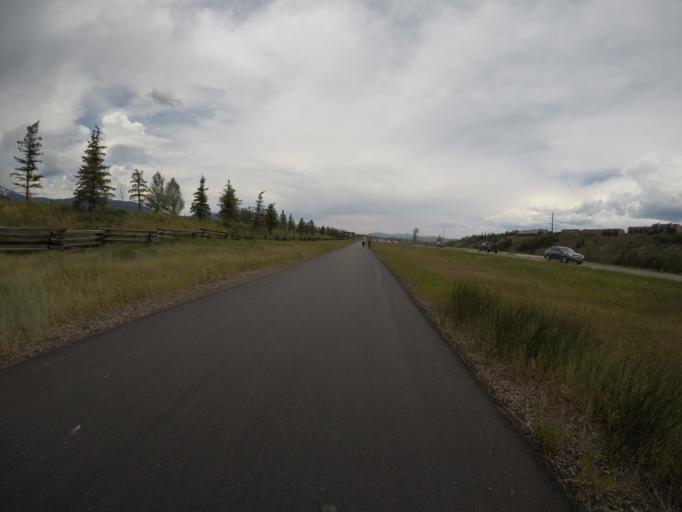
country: US
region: Colorado
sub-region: Grand County
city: Fraser
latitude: 39.9381
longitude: -105.7995
